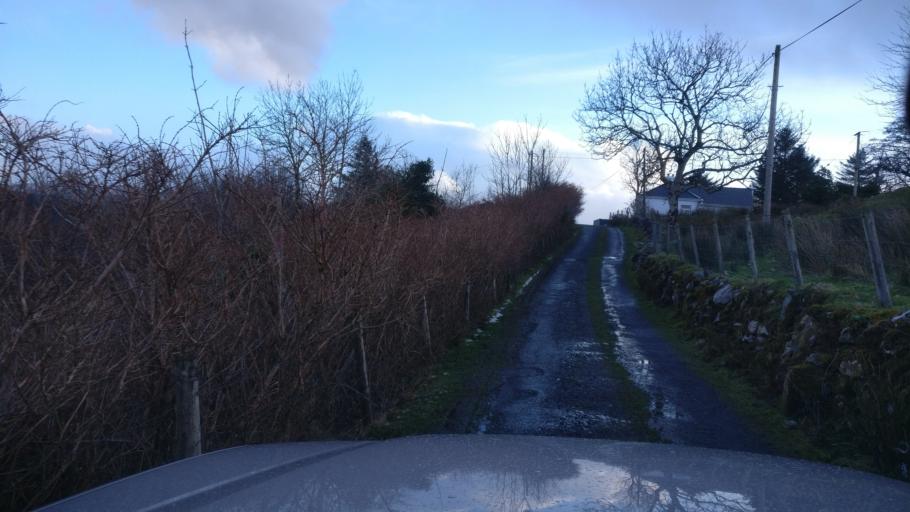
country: IE
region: Connaught
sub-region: County Galway
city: Clifden
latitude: 53.4870
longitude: -9.6980
